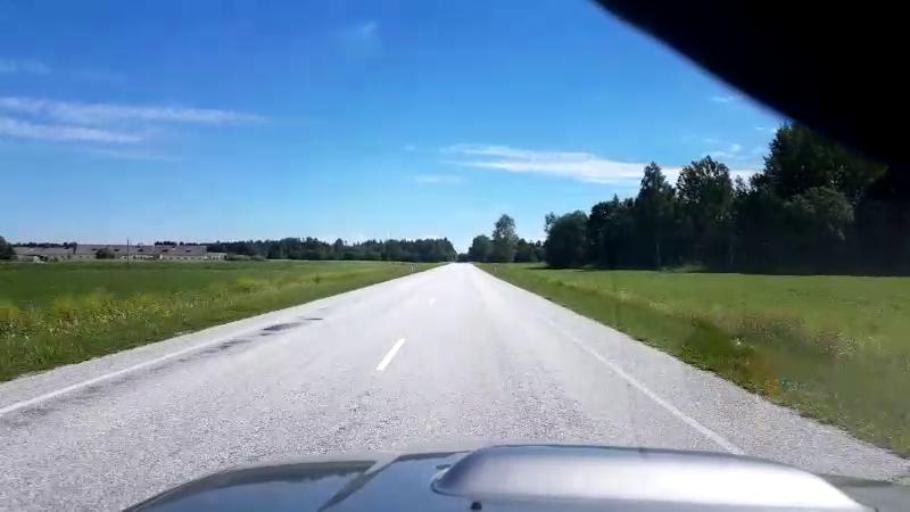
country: EE
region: Laeaene-Virumaa
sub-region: Rakke vald
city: Rakke
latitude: 58.9547
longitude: 26.1731
